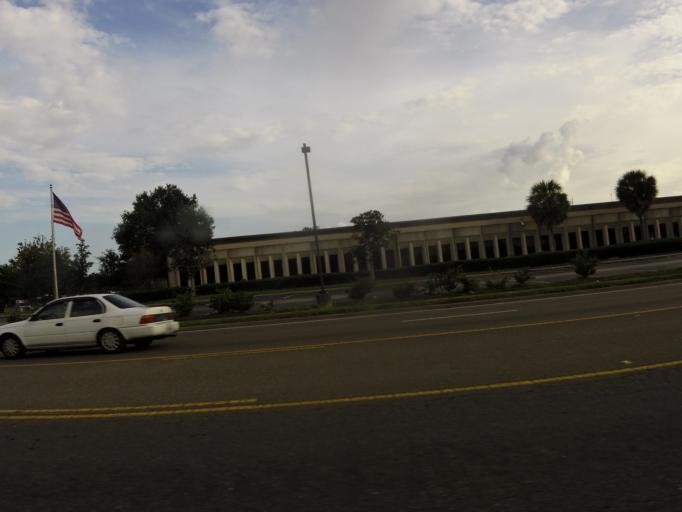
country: US
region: Florida
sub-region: Duval County
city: Jacksonville
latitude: 30.3358
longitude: -81.7564
